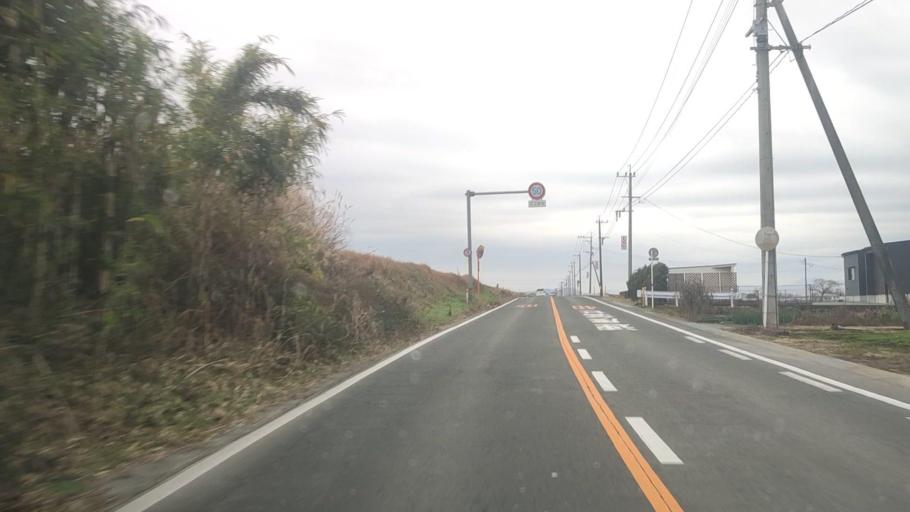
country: JP
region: Kumamoto
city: Ozu
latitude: 32.8504
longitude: 130.8465
